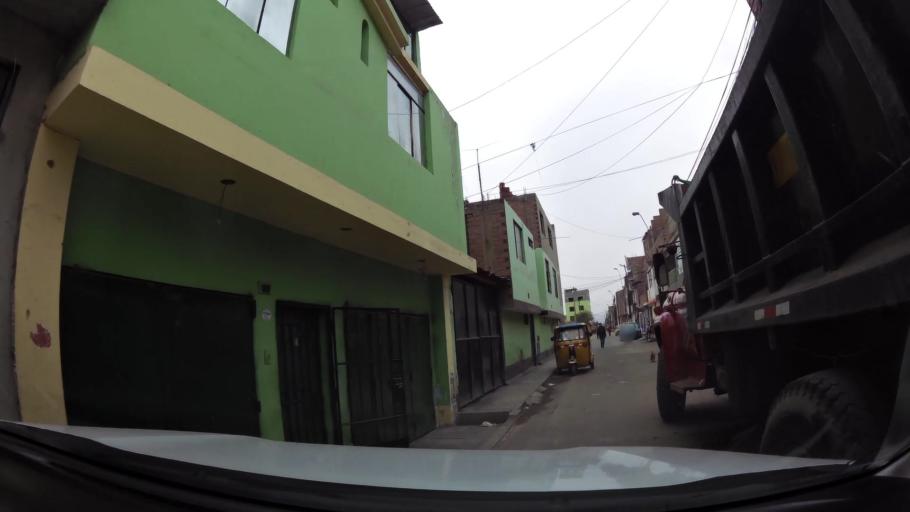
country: PE
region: Lima
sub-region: Lima
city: Surco
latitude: -12.1737
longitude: -76.9684
